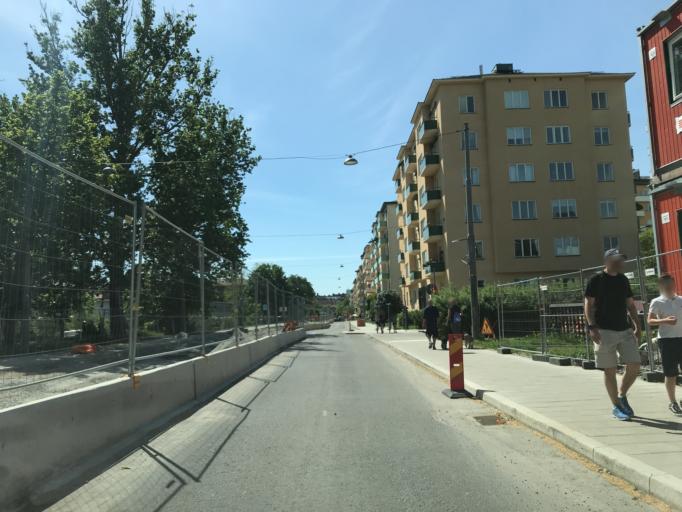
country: SE
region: Stockholm
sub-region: Stockholms Kommun
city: OEstermalm
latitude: 59.3437
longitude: 18.0999
